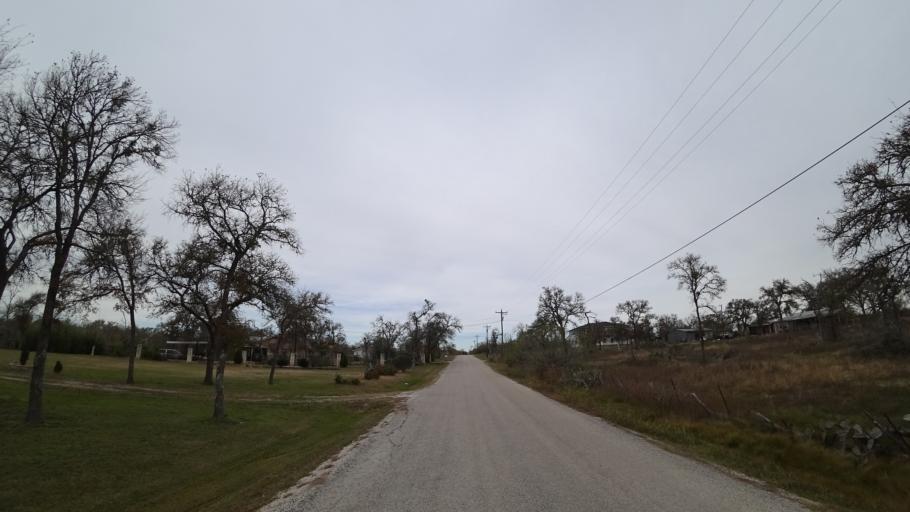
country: US
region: Texas
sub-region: Travis County
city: Garfield
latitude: 30.1009
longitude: -97.5762
